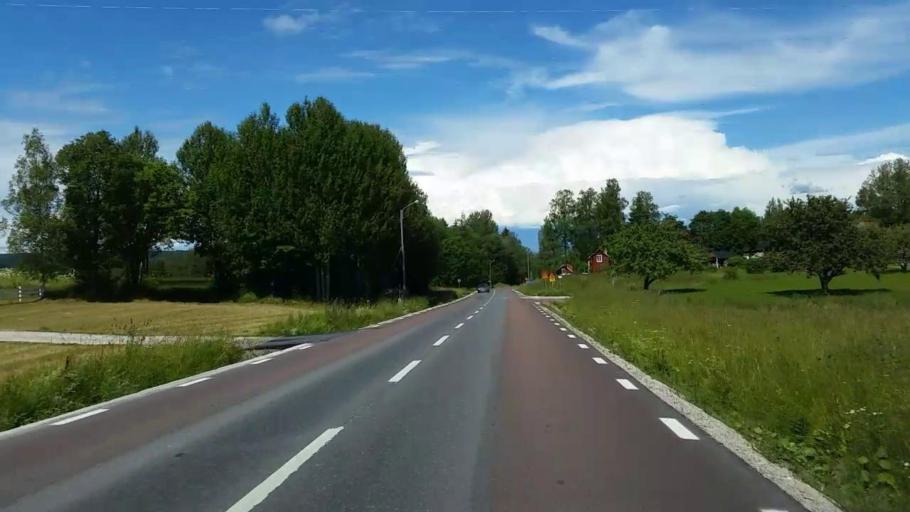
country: SE
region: Dalarna
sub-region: Rattviks Kommun
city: Raettvik
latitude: 61.0416
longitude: 15.1953
